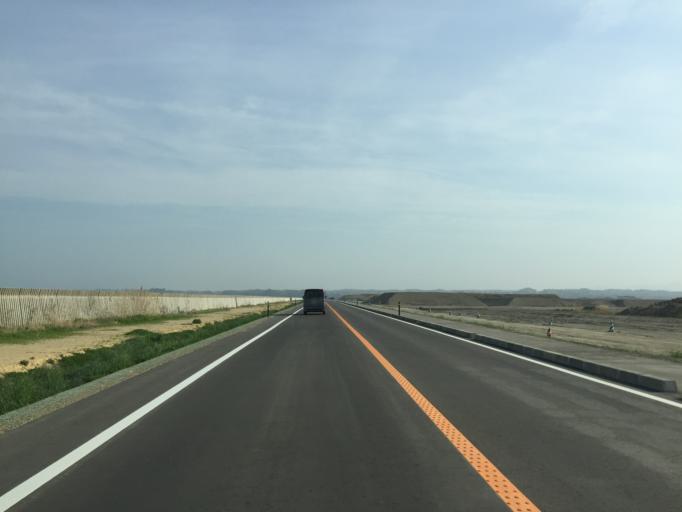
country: JP
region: Miyagi
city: Marumori
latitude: 37.7864
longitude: 140.9841
